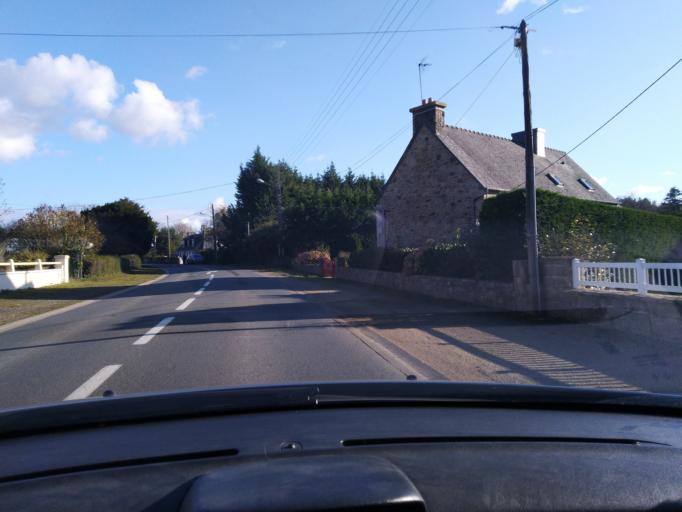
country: FR
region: Brittany
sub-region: Departement des Cotes-d'Armor
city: Plestin-les-Greves
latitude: 48.6423
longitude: -3.6260
